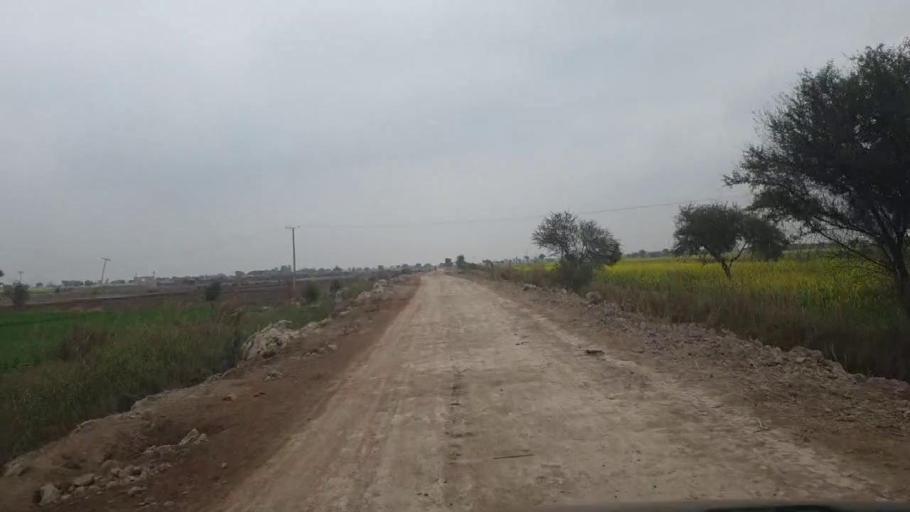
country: PK
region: Sindh
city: Shahdadpur
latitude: 25.9062
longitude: 68.7109
